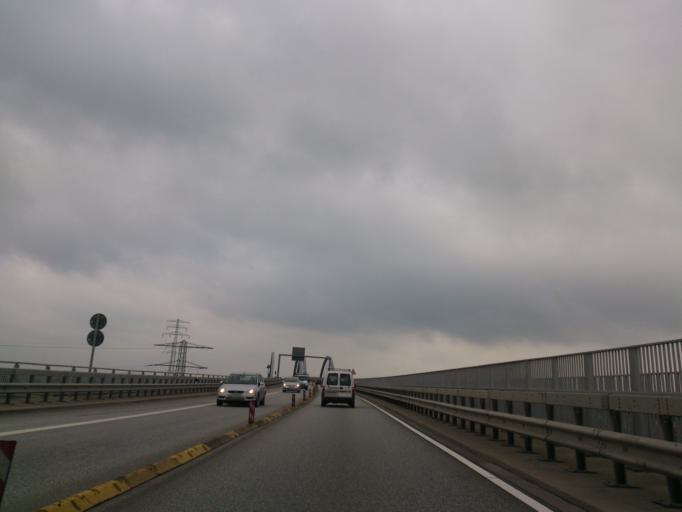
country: DE
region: Schleswig-Holstein
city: Heiligenstedten
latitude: 53.9305
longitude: 9.4807
